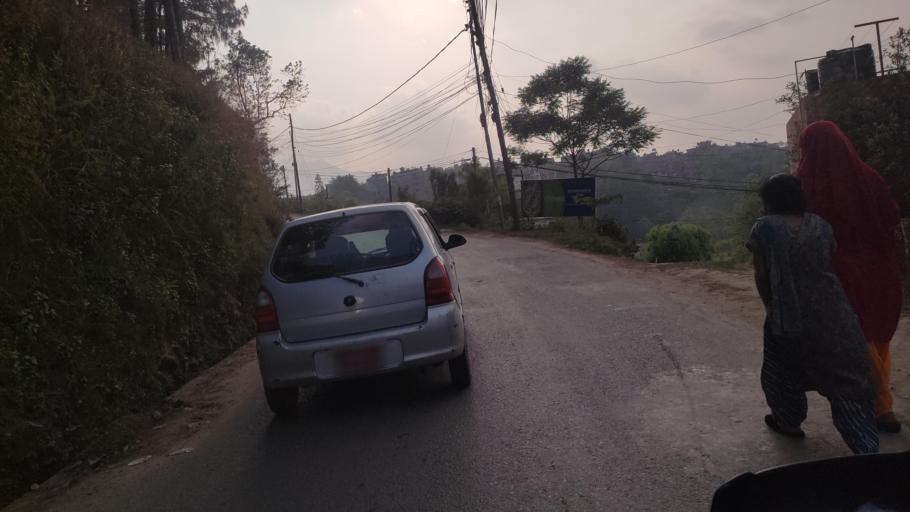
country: NP
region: Central Region
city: Kirtipur
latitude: 27.6708
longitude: 85.2893
